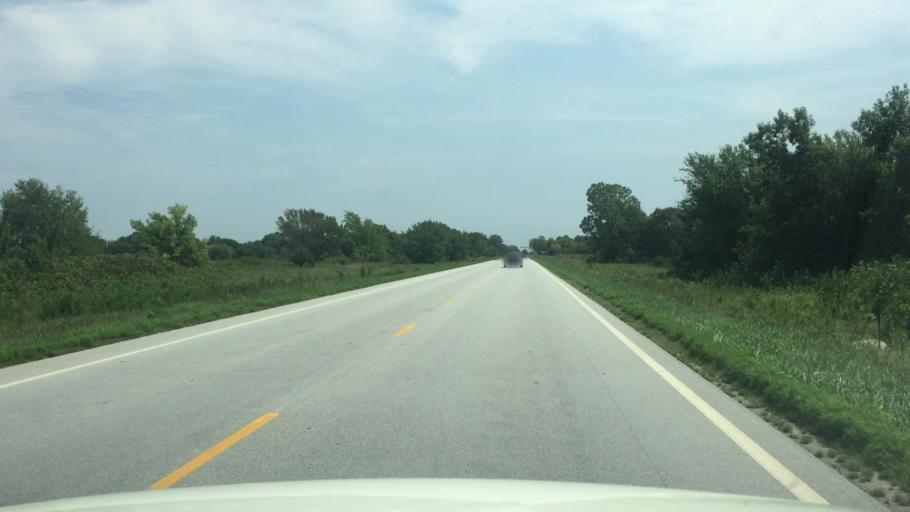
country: US
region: Kansas
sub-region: Cherokee County
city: Columbus
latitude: 37.1796
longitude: -94.9553
